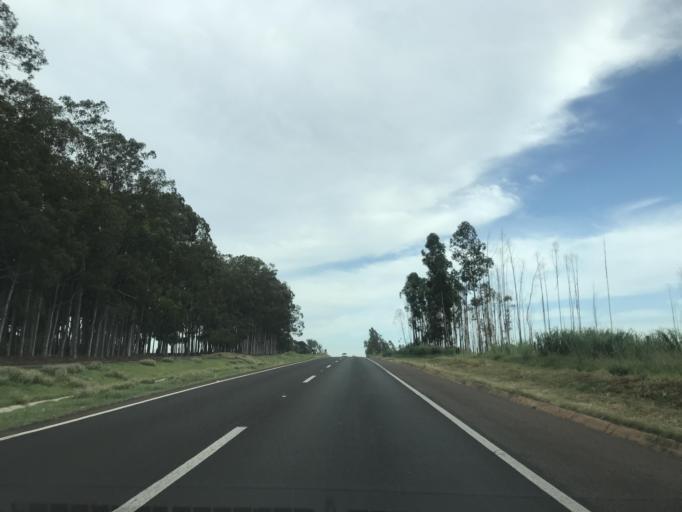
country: BR
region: Parana
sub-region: Alto Parana
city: Alto Parana
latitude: -23.1537
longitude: -52.2688
